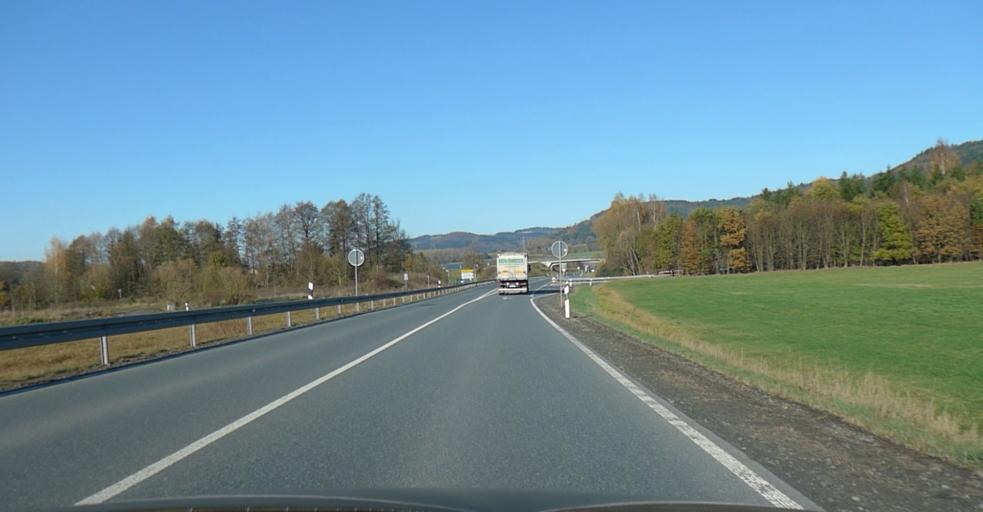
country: DE
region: Bavaria
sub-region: Upper Franconia
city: Untersteinach
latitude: 50.1340
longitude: 11.5369
